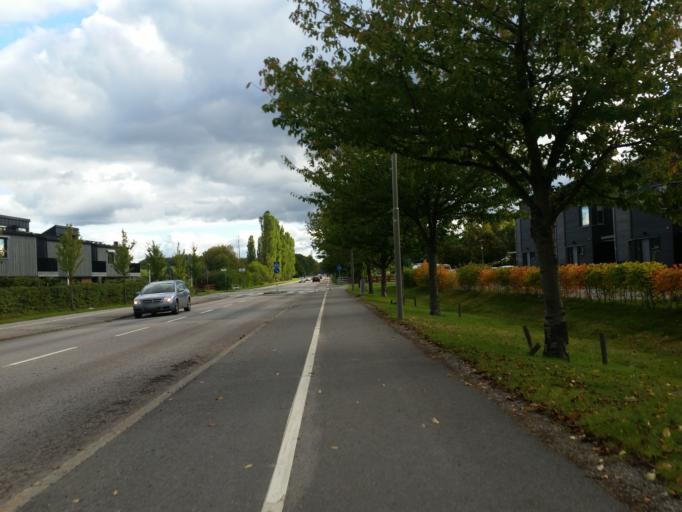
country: SE
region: Stockholm
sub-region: Nacka Kommun
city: Nacka
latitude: 59.2704
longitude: 18.1129
